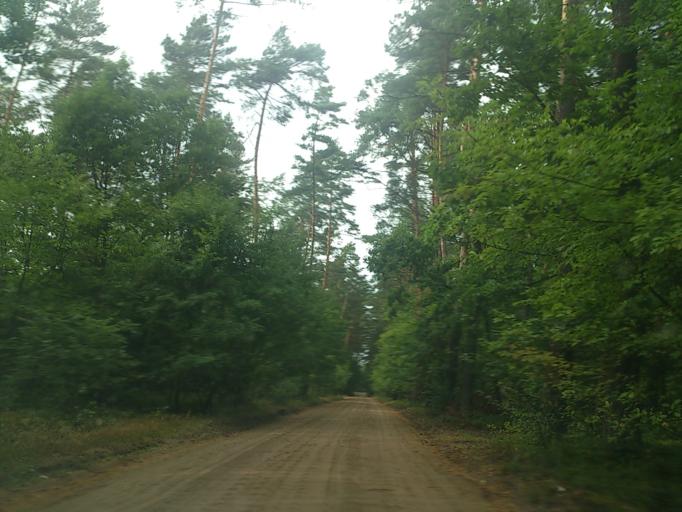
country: PL
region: Greater Poland Voivodeship
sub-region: Powiat poznanski
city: Kobylnica
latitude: 52.5259
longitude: 17.1225
